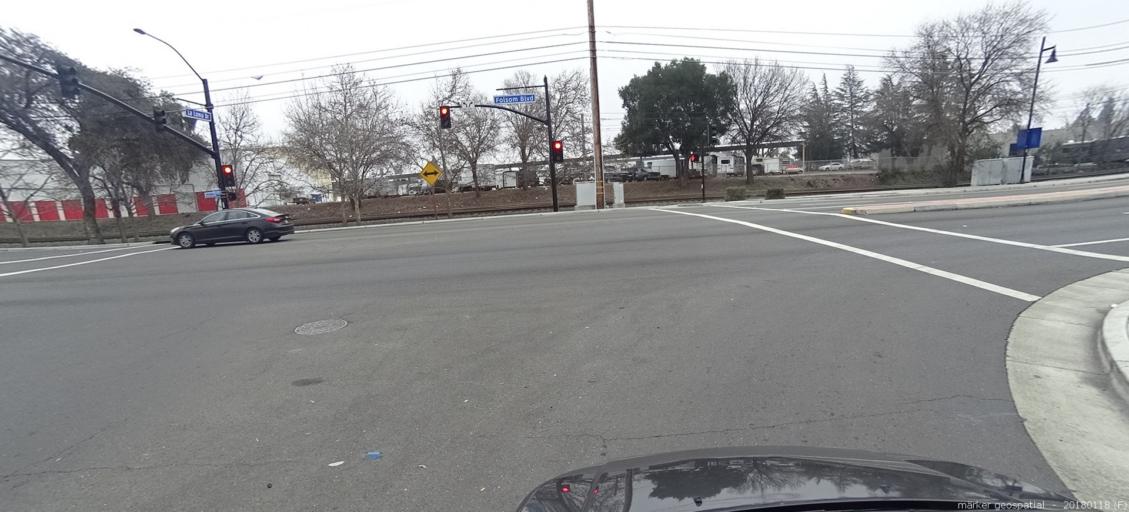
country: US
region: California
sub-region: Sacramento County
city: Rancho Cordova
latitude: 38.5843
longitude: -121.3136
